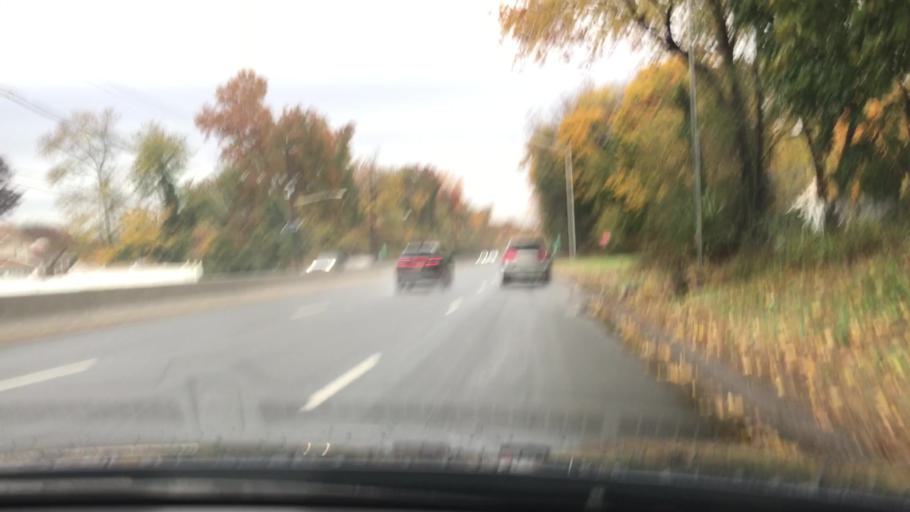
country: US
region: New Jersey
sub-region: Bergen County
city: Teaneck
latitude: 40.8978
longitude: -74.0233
